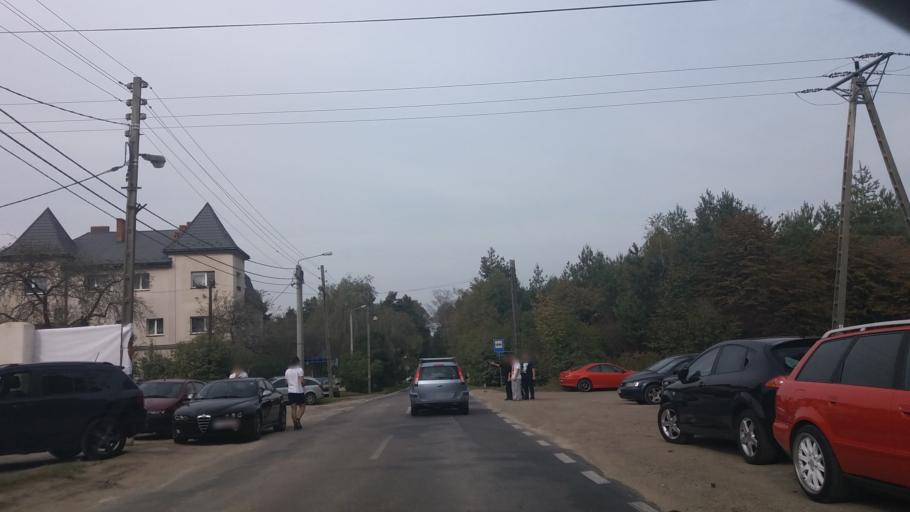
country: PL
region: Lesser Poland Voivodeship
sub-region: Powiat chrzanowski
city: Pogorzyce
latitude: 50.1125
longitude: 19.4428
